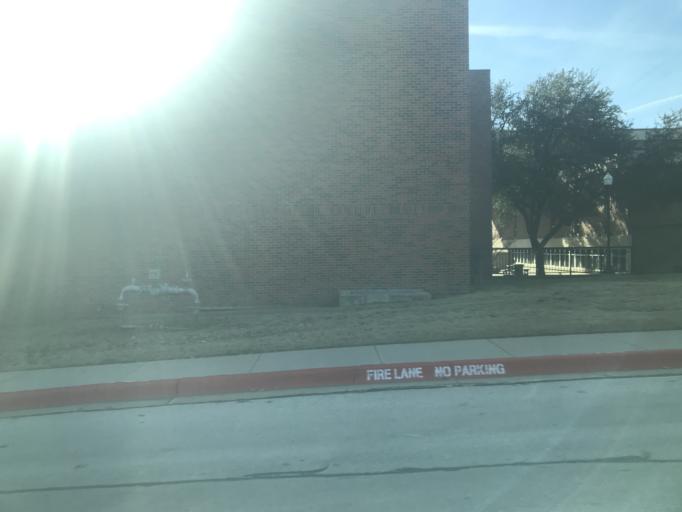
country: US
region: Texas
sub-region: Taylor County
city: Abilene
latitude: 32.4788
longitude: -99.7333
